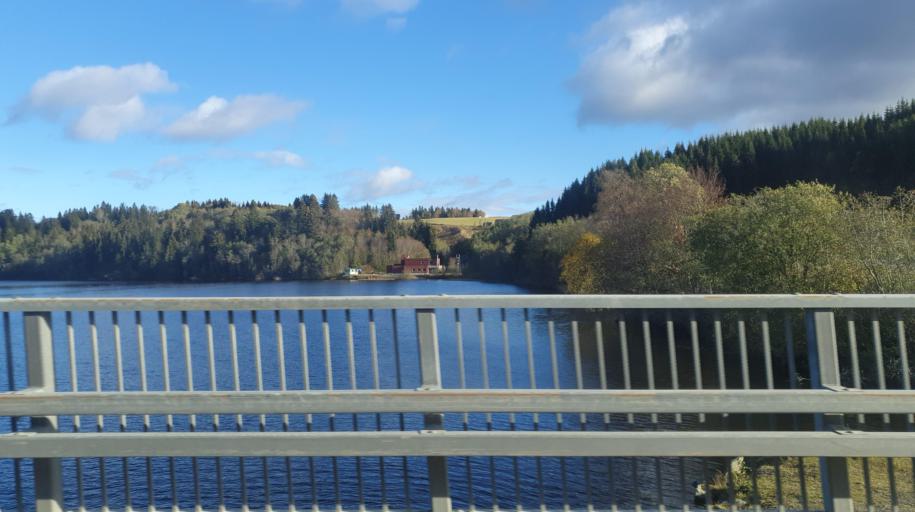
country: NO
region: Sor-Trondelag
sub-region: Klaebu
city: Klaebu
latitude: 63.3104
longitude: 10.4533
